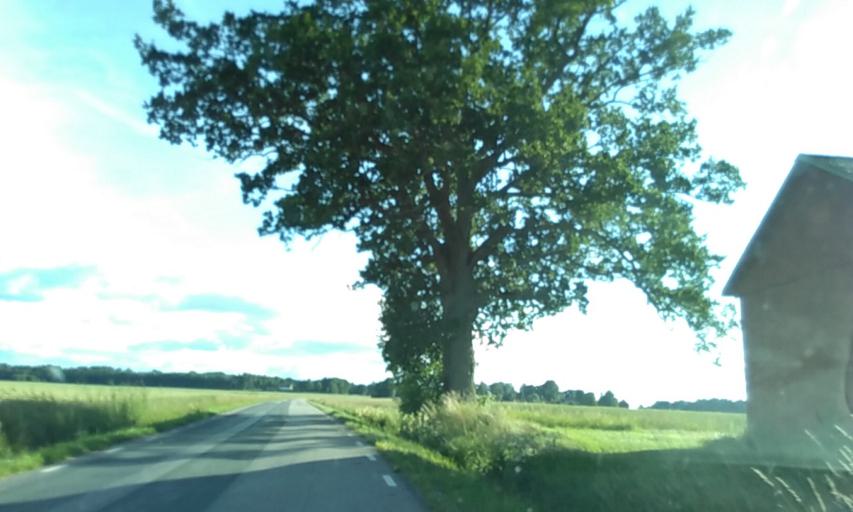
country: SE
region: Vaestra Goetaland
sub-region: Vara Kommun
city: Vara
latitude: 58.3705
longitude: 12.8767
